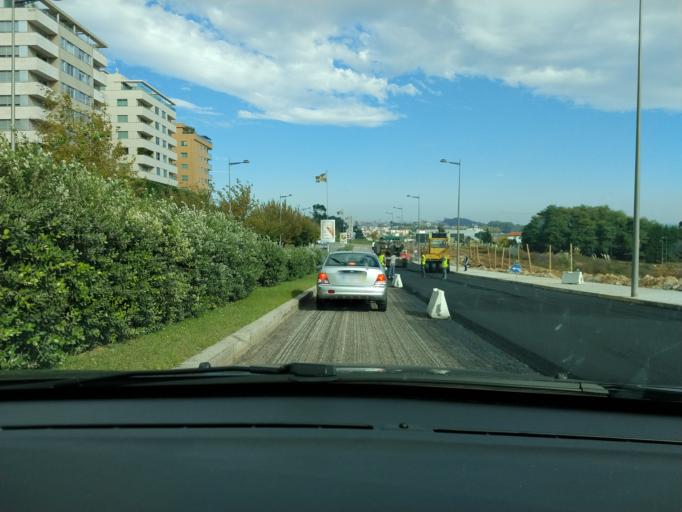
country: PT
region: Porto
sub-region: Vila Nova de Gaia
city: Oliveira do Douro
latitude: 41.1230
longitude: -8.5984
